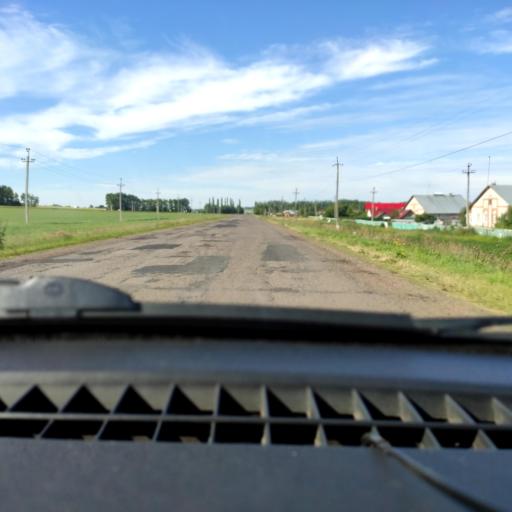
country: RU
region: Bashkortostan
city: Karmaskaly
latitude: 54.3942
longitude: 56.2427
